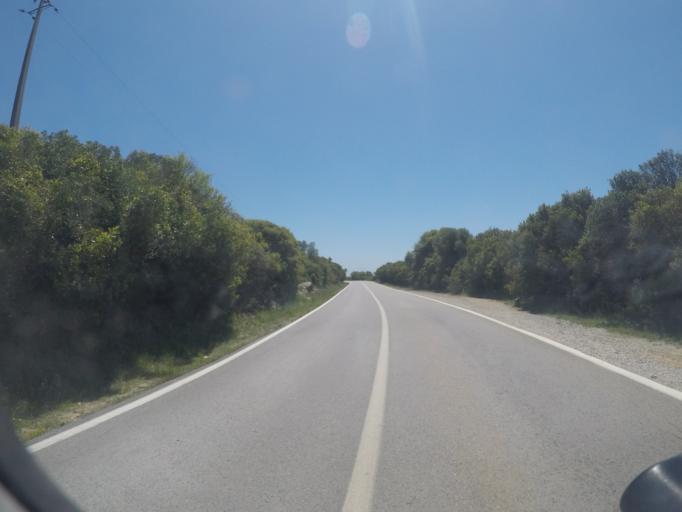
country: PT
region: Setubal
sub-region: Sesimbra
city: Sesimbra
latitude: 38.4643
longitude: -9.0271
